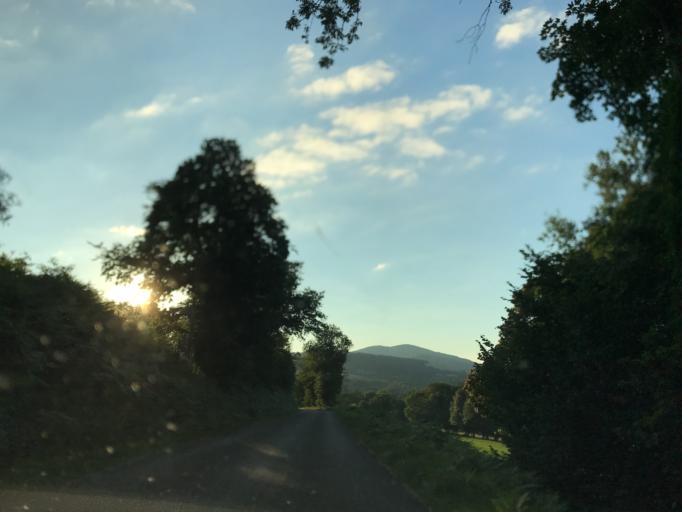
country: FR
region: Rhone-Alpes
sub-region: Departement de la Loire
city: Noiretable
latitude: 45.7927
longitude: 3.7762
